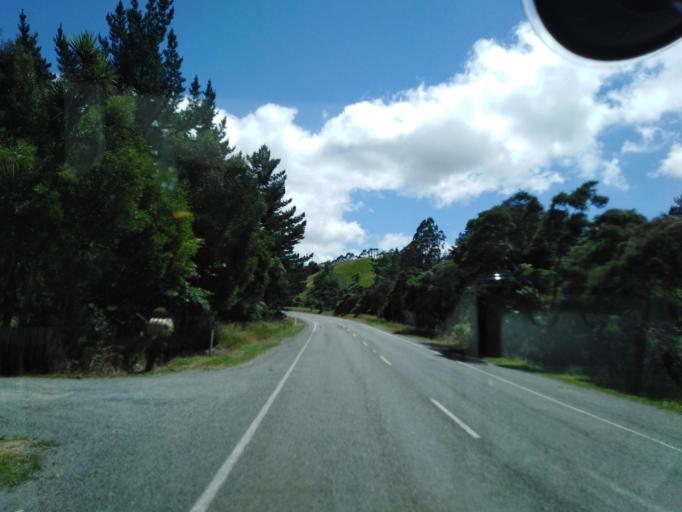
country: NZ
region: Nelson
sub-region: Nelson City
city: Nelson
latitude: -41.2215
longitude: 173.3976
